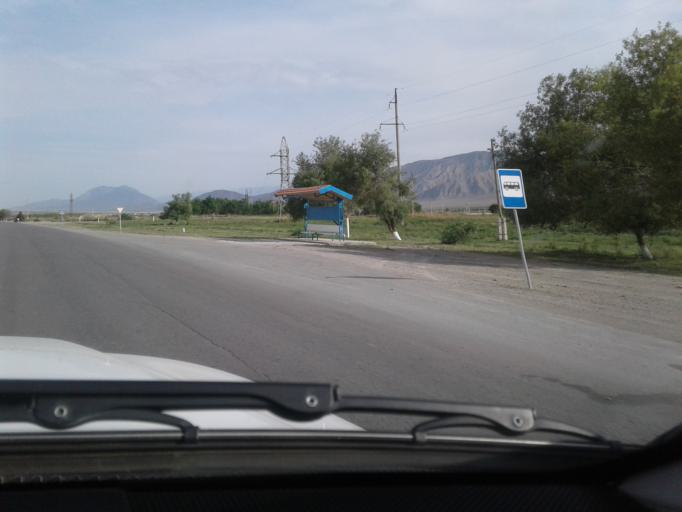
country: TM
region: Ahal
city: Arcabil
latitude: 38.1923
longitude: 57.8405
